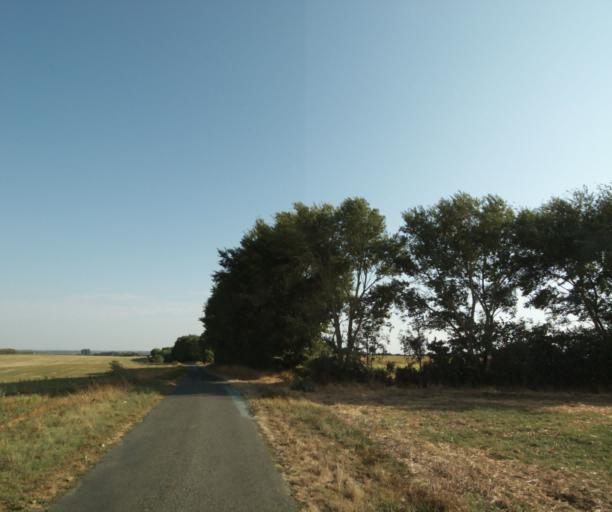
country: FR
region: Poitou-Charentes
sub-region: Departement de la Charente-Maritime
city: Cabariot
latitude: 45.9707
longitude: -0.8284
